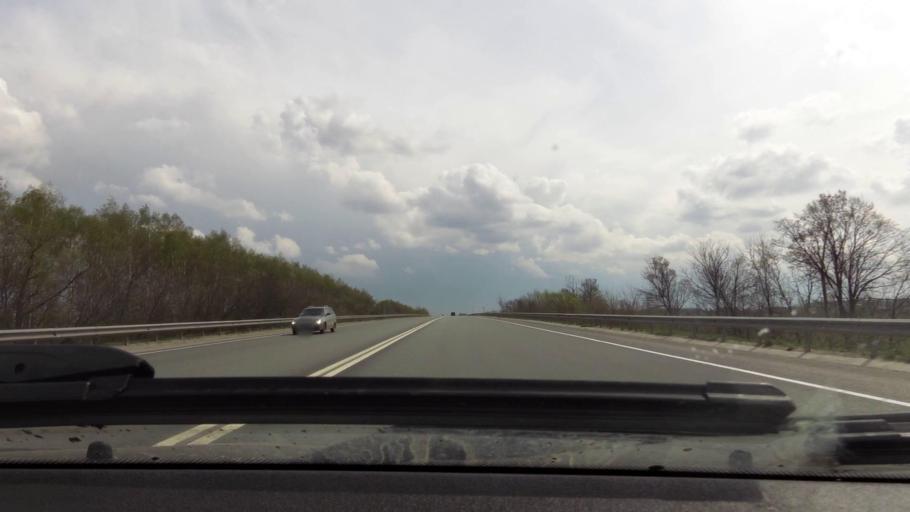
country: RU
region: Rjazan
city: Bagramovo
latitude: 54.7380
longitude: 39.4489
